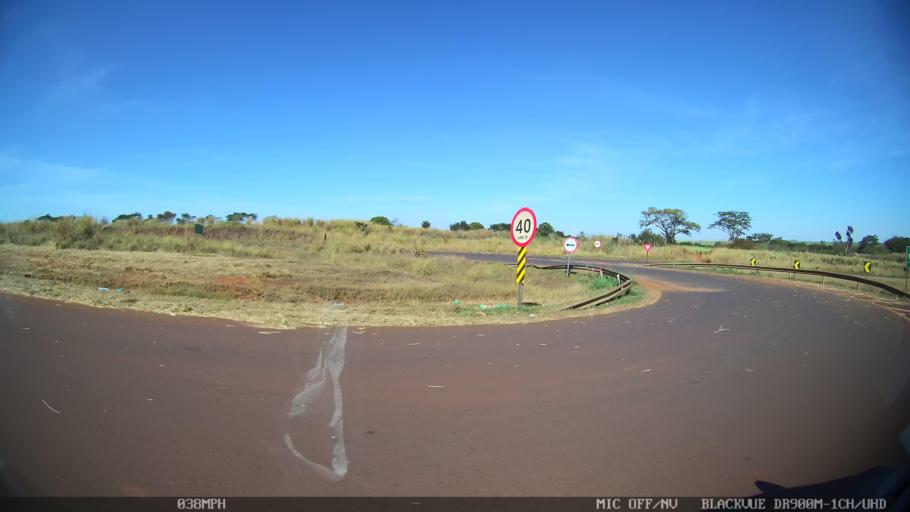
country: BR
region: Sao Paulo
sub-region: Barretos
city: Barretos
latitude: -20.4489
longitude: -48.4525
